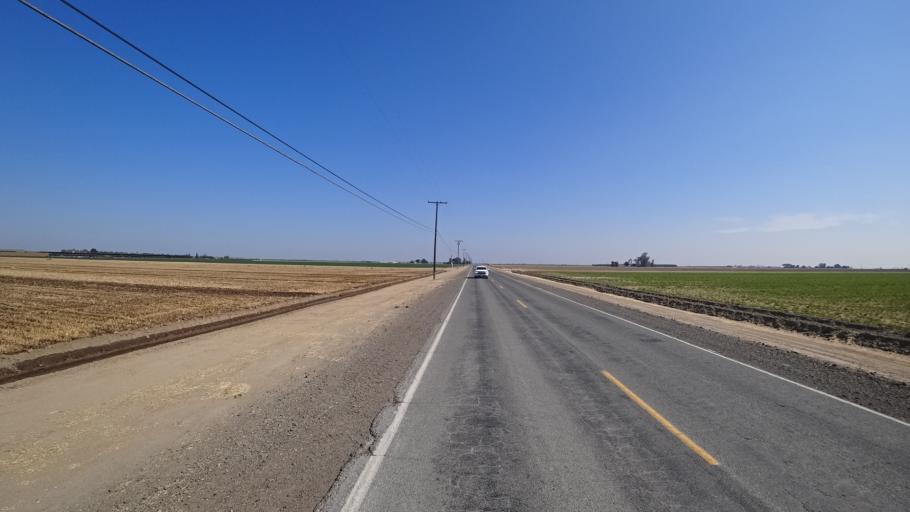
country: US
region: California
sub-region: Kings County
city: Hanford
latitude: 36.3634
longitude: -119.5651
